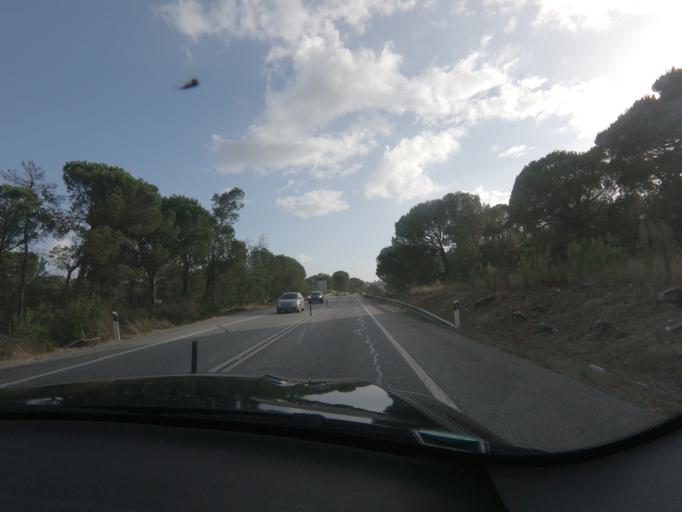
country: PT
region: Viseu
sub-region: Concelho de Tondela
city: Tondela
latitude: 40.5304
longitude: -8.0665
